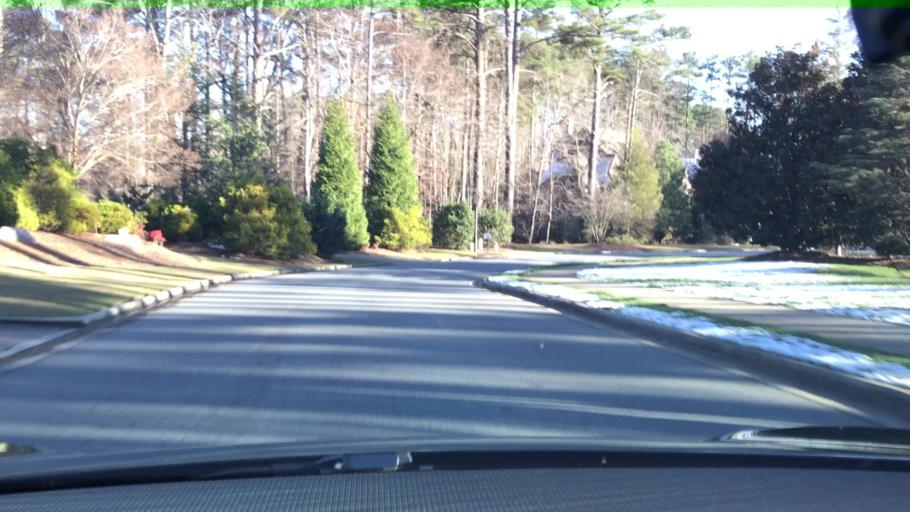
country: US
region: Georgia
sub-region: Gwinnett County
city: Suwanee
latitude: 34.0745
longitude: -84.0986
